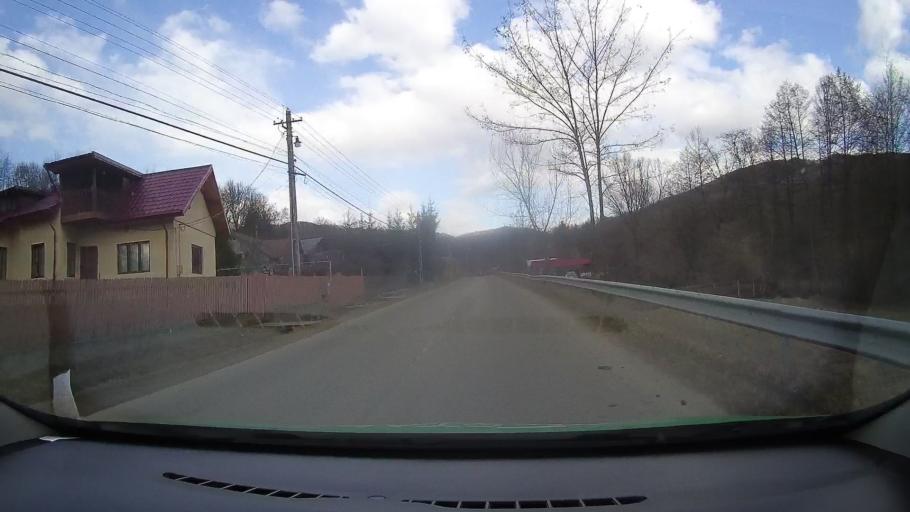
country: RO
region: Dambovita
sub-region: Comuna Visinesti
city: Visinesti
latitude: 45.0703
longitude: 25.5461
